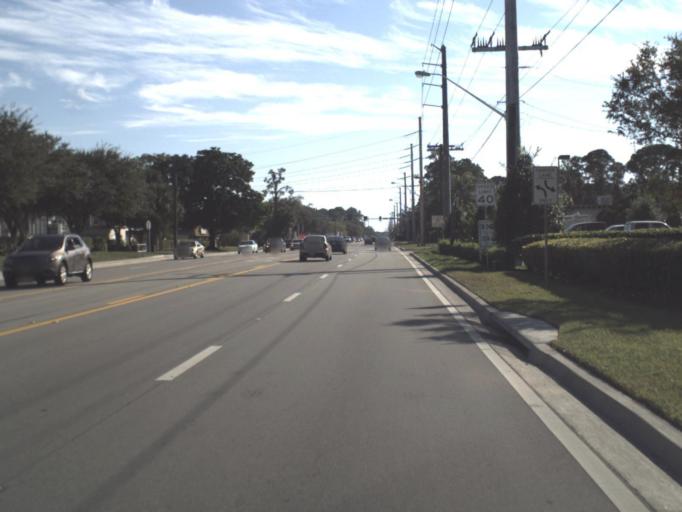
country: US
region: Florida
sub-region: Brevard County
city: June Park
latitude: 28.0971
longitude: -80.6727
